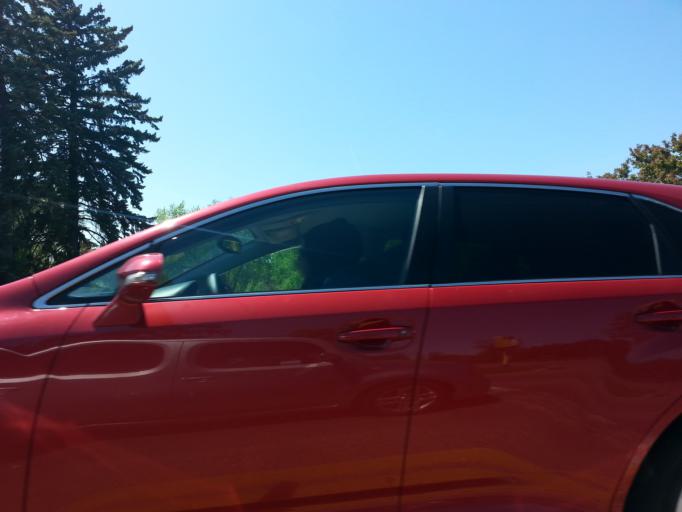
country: US
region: Minnesota
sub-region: Hennepin County
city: Richfield
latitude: 44.9012
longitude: -93.2475
